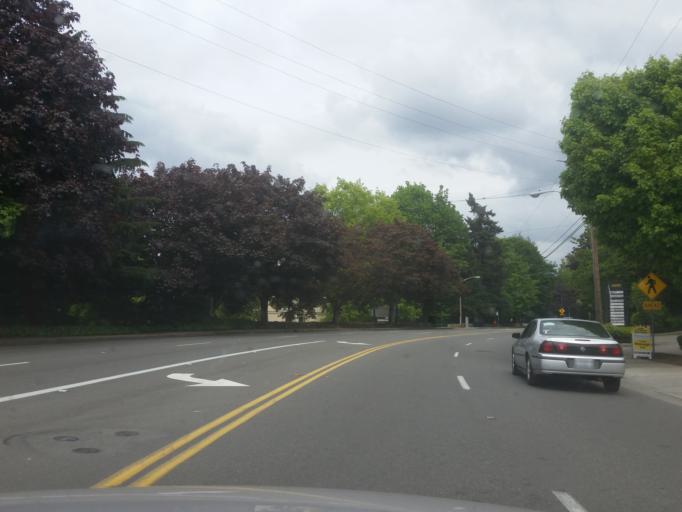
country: US
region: Washington
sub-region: King County
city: Inglewood-Finn Hill
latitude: 47.7082
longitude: -122.2102
